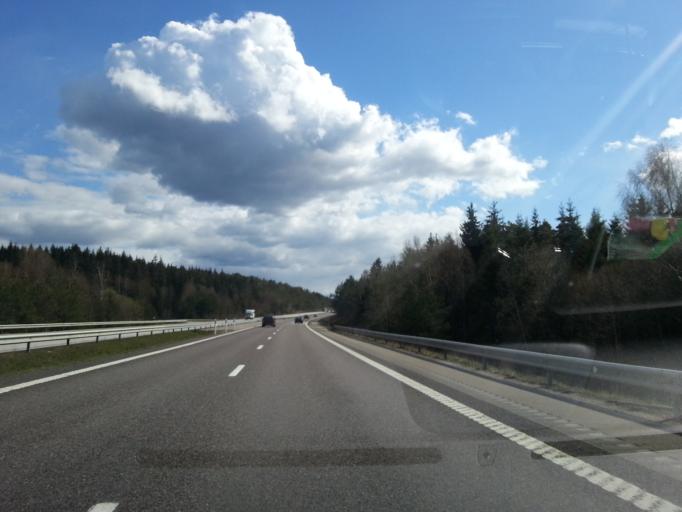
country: SE
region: Vaestra Goetaland
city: Svanesund
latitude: 58.1033
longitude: 11.8807
